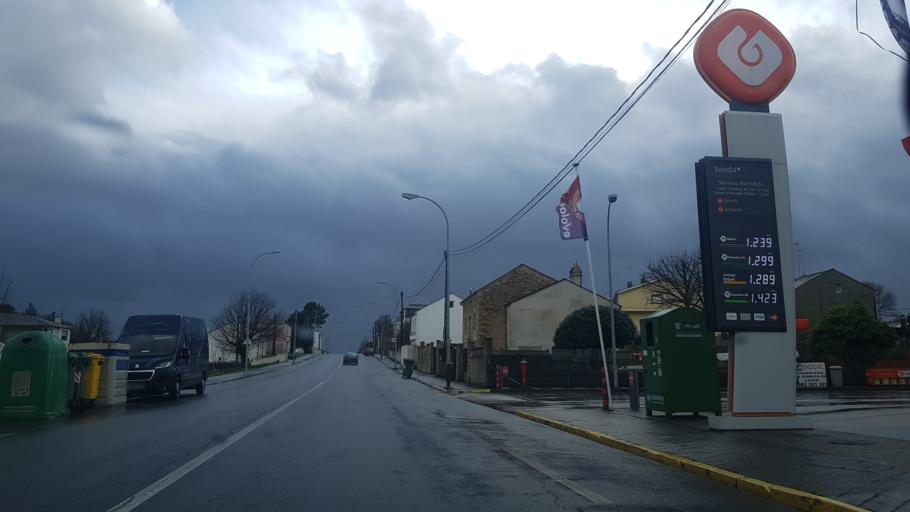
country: ES
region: Galicia
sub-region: Provincia de Lugo
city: Vilalba
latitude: 43.2890
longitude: -7.6790
